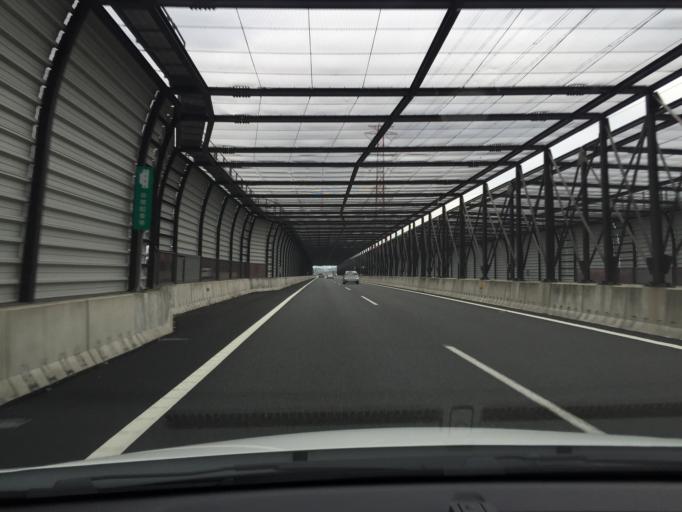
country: JP
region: Saitama
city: Sakado
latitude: 35.9761
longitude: 139.4558
